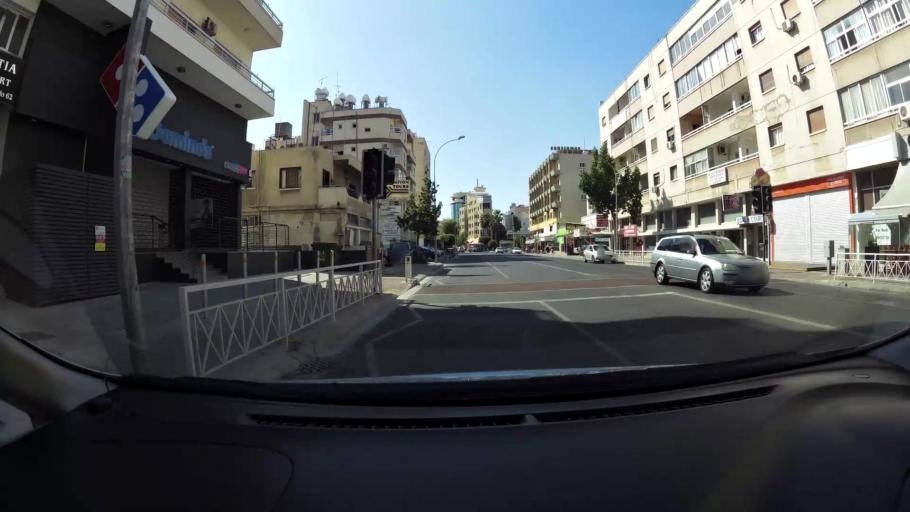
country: CY
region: Larnaka
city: Larnaca
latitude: 34.9277
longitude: 33.6369
